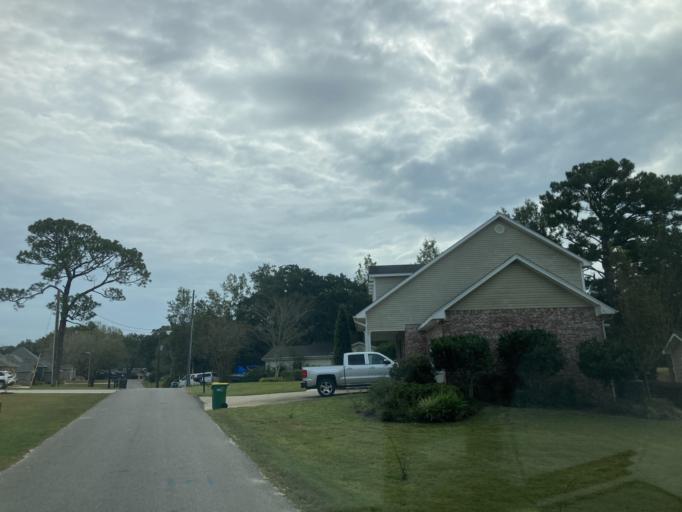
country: US
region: Mississippi
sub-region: Jackson County
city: Gulf Hills
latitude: 30.4345
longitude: -88.8391
